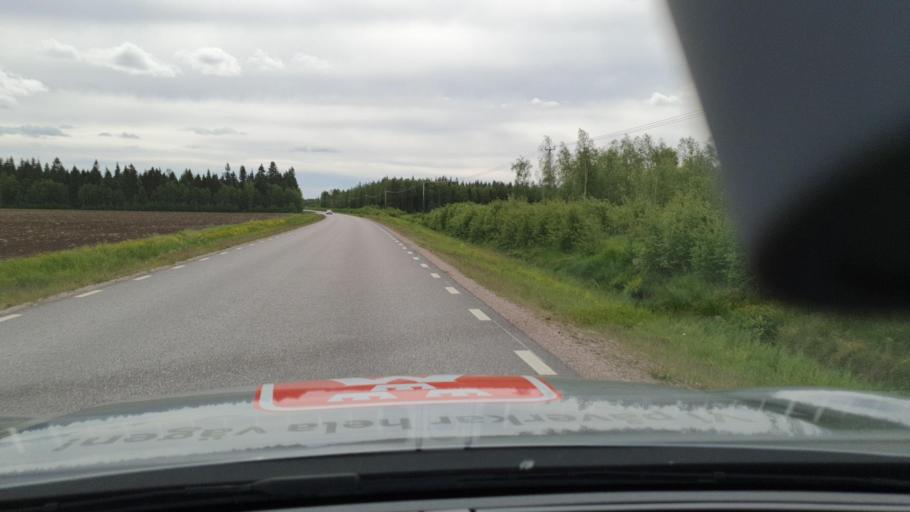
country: SE
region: Norrbotten
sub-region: Kalix Kommun
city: Kalix
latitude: 65.8984
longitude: 23.4613
